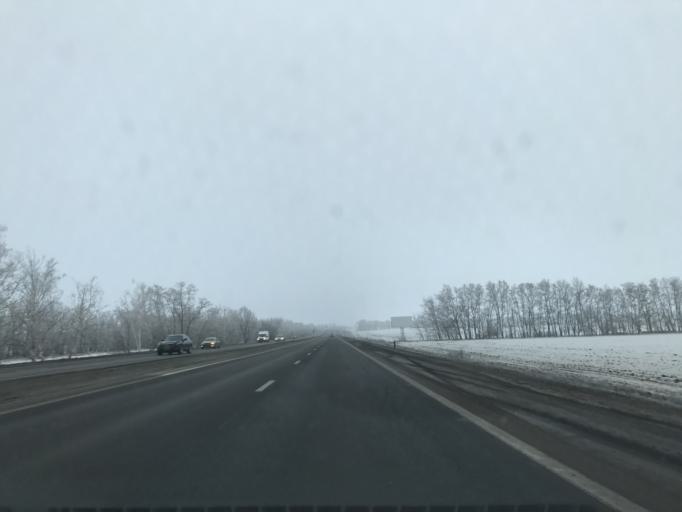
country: RU
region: Rostov
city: Grushevskaya
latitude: 47.4764
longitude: 39.9715
